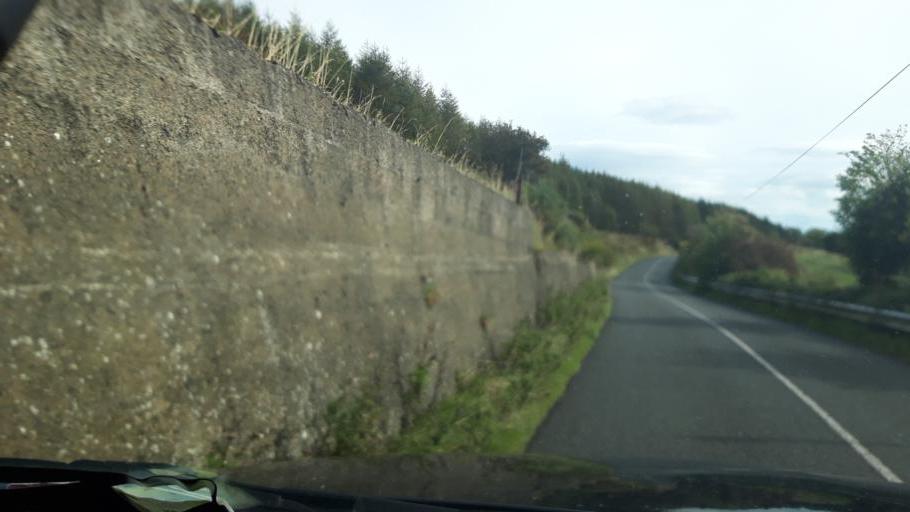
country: IE
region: Leinster
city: Ballinteer
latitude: 53.2286
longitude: -6.2646
